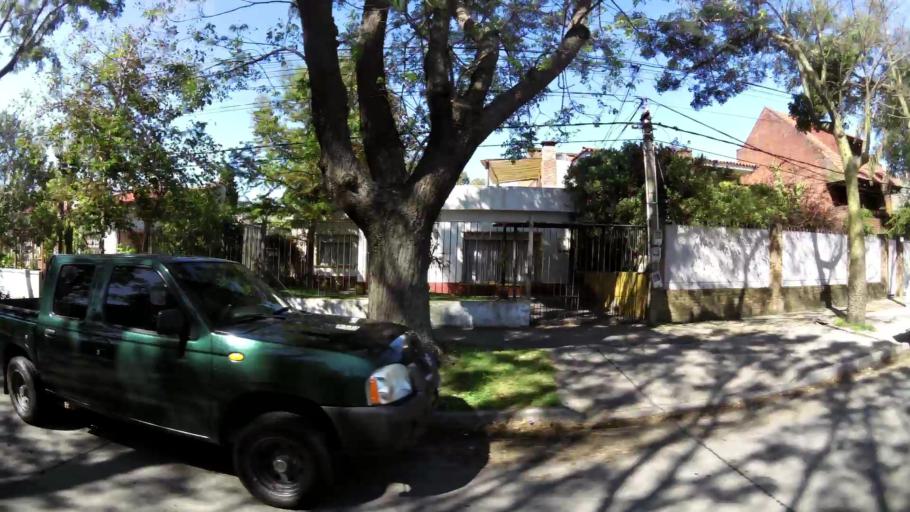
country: UY
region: Canelones
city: Paso de Carrasco
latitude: -34.8922
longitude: -56.0937
